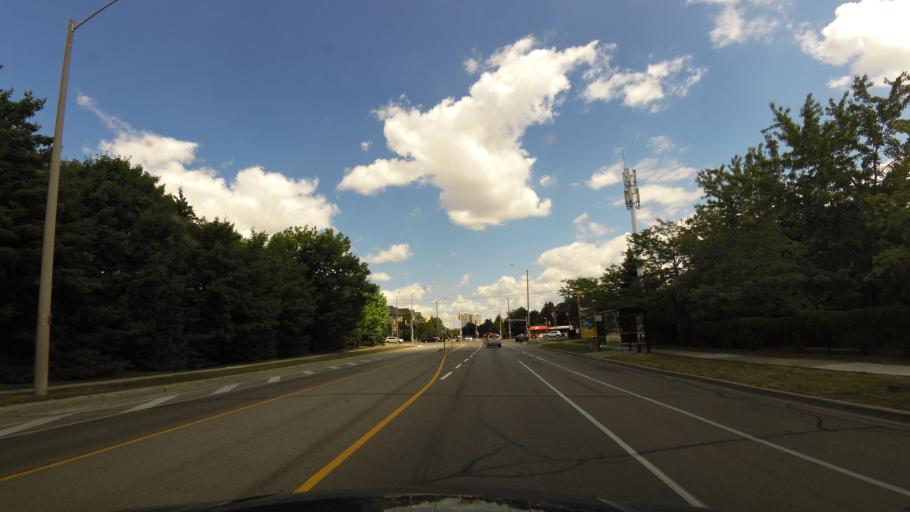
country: CA
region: Ontario
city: Mississauga
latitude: 43.6021
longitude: -79.6723
